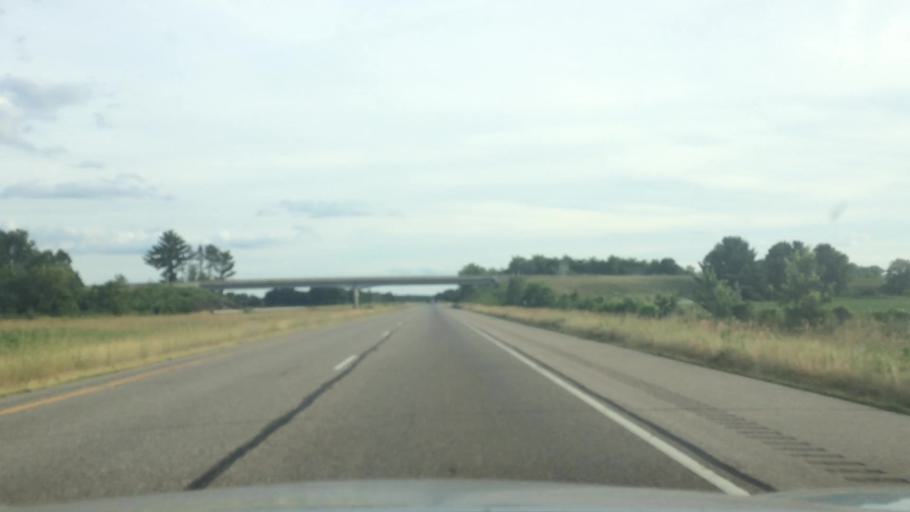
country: US
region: Wisconsin
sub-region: Waushara County
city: Wautoma
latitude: 44.1866
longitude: -89.5263
